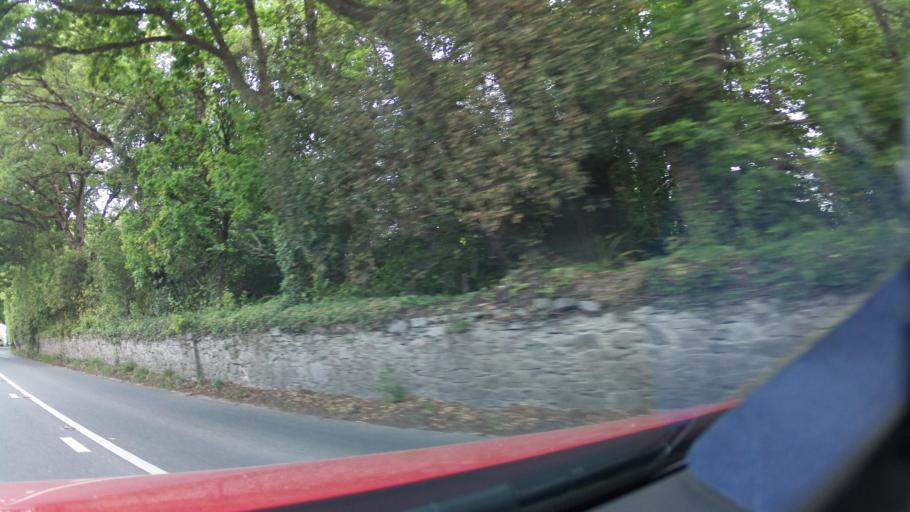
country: GB
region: England
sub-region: Devon
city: Newton Abbot
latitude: 50.5521
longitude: -3.6412
